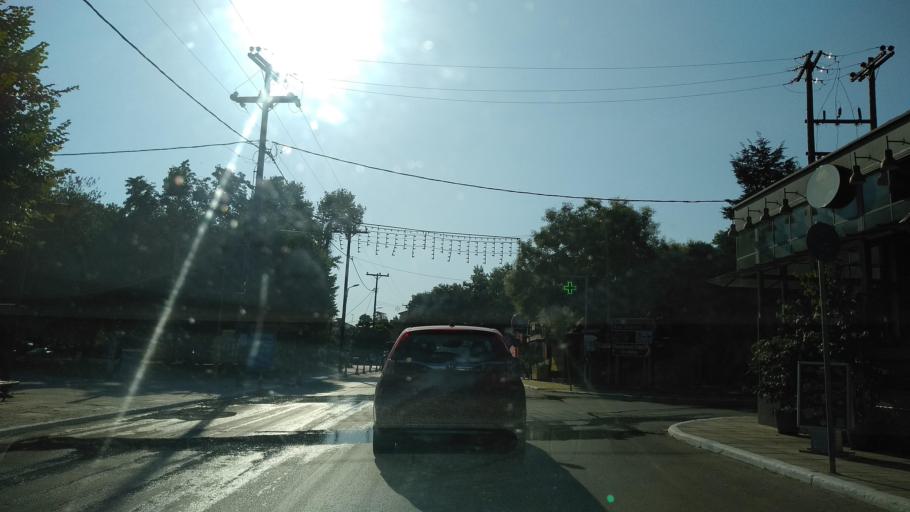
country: GR
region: Central Macedonia
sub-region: Nomos Thessalonikis
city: Stavros
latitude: 40.6650
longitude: 23.7005
